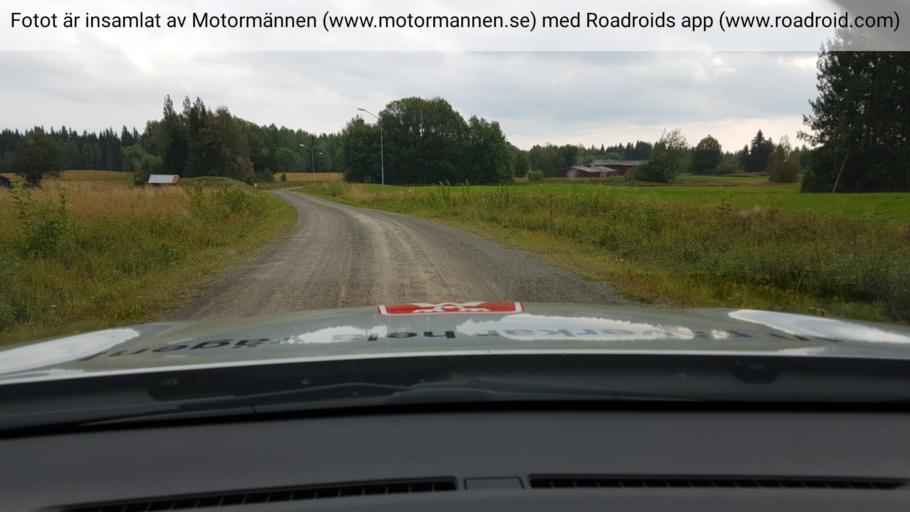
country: SE
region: Jaemtland
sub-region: Stroemsunds Kommun
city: Stroemsund
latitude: 63.7769
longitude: 15.3173
